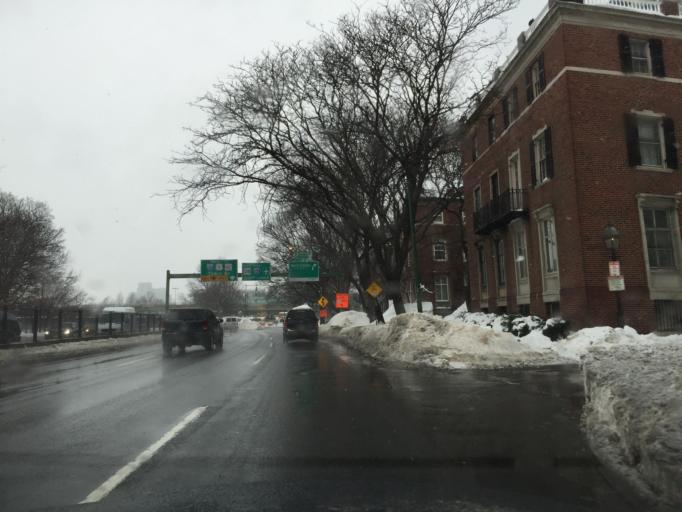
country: US
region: Massachusetts
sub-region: Suffolk County
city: Boston
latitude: 42.3593
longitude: -71.0721
